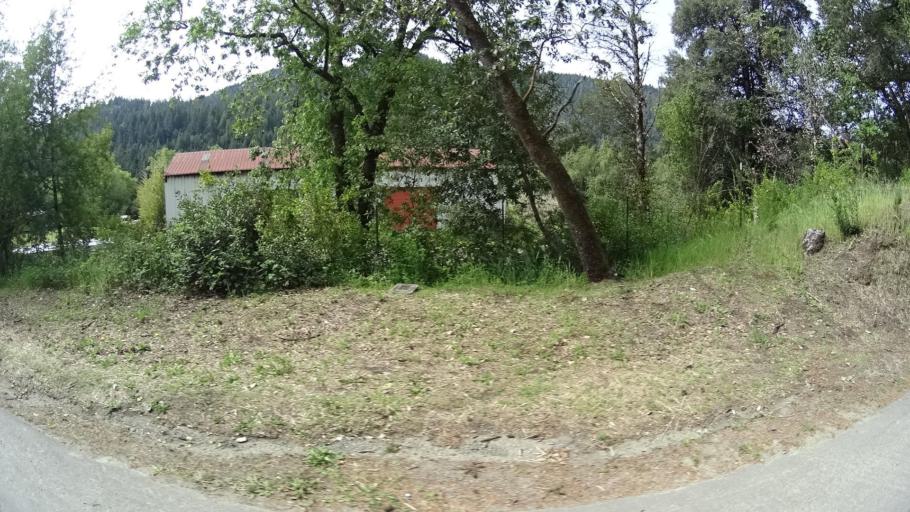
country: US
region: California
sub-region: Humboldt County
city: Redway
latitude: 40.1165
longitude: -123.8175
